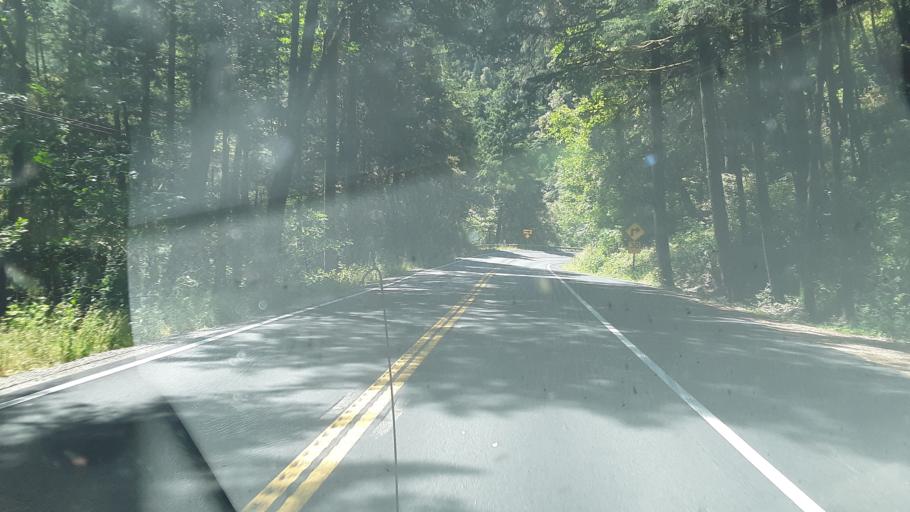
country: US
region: California
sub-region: Del Norte County
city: Bertsch-Oceanview
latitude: 41.8240
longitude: -124.0317
